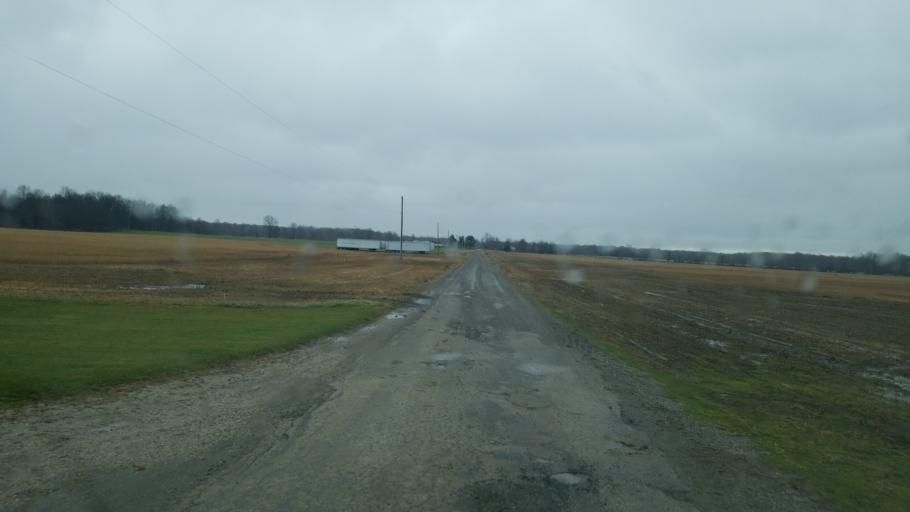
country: US
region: Ohio
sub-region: Ashtabula County
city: Roaming Shores
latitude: 41.5810
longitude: -80.7193
